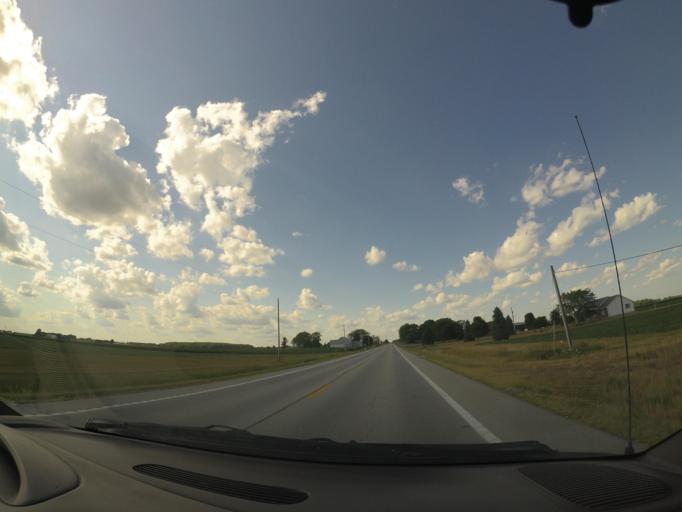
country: US
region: Ohio
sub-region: Wood County
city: Pemberville
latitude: 41.3647
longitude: -83.4168
